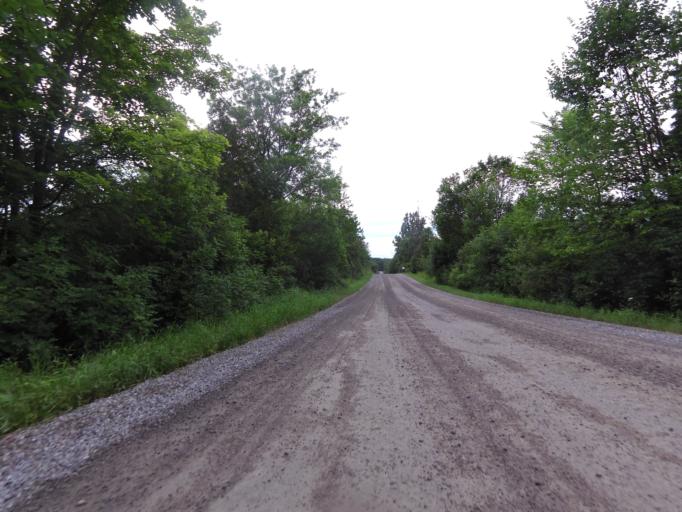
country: CA
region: Ontario
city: Carleton Place
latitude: 45.1530
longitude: -76.2362
